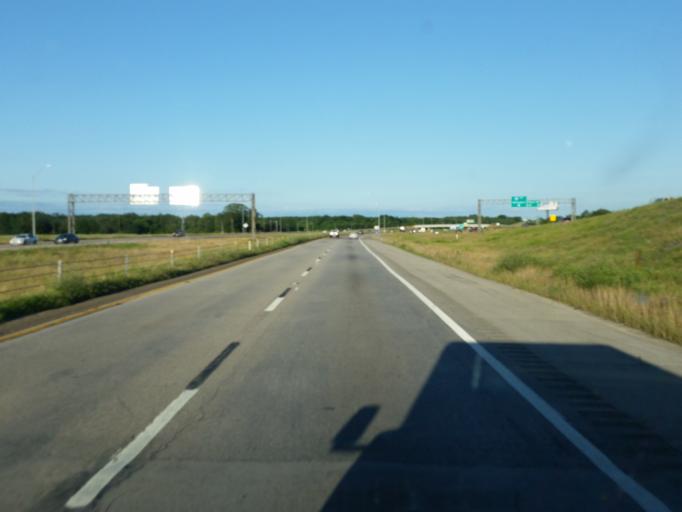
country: US
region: Texas
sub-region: Kaufman County
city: Terrell
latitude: 32.7143
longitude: -96.3090
